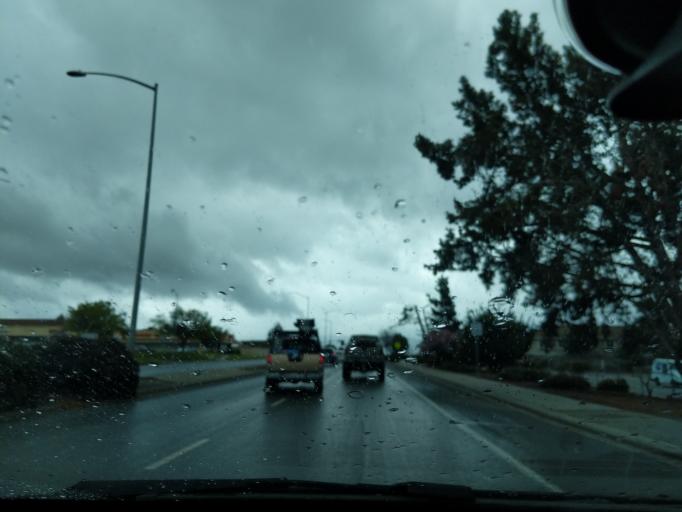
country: US
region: California
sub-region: Monterey County
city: Boronda
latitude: 36.6958
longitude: -121.6688
